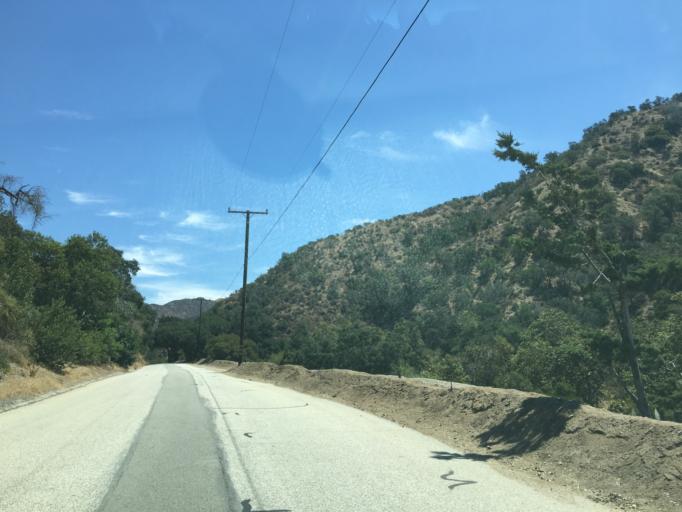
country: US
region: California
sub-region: Los Angeles County
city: Glendora
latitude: 34.1576
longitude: -117.8305
